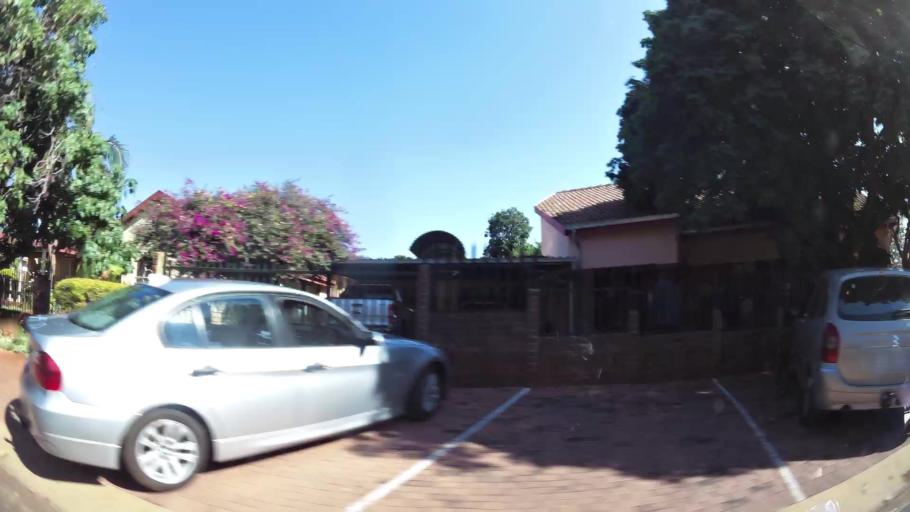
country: ZA
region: Gauteng
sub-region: City of Tshwane Metropolitan Municipality
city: Pretoria
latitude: -25.6810
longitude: 28.2356
